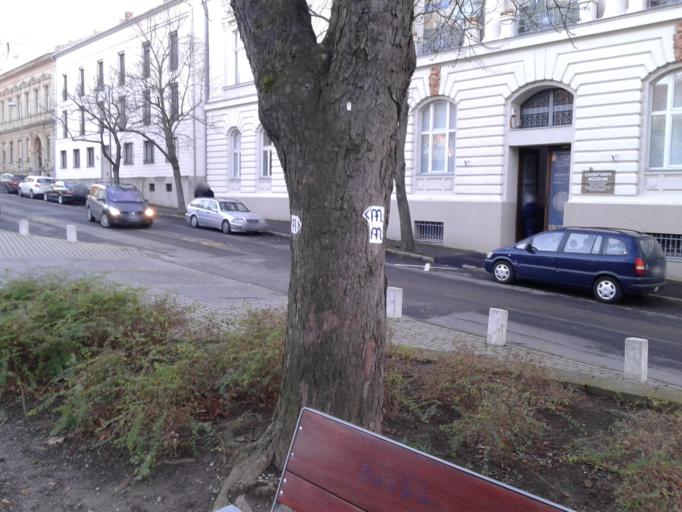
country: HU
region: Baranya
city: Pecs
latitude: 46.0776
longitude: 18.2250
